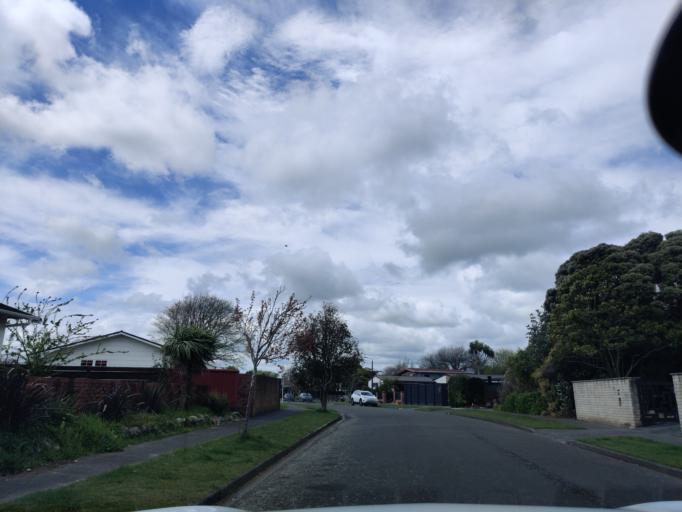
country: NZ
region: Manawatu-Wanganui
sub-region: Palmerston North City
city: Palmerston North
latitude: -40.3807
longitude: 175.5944
